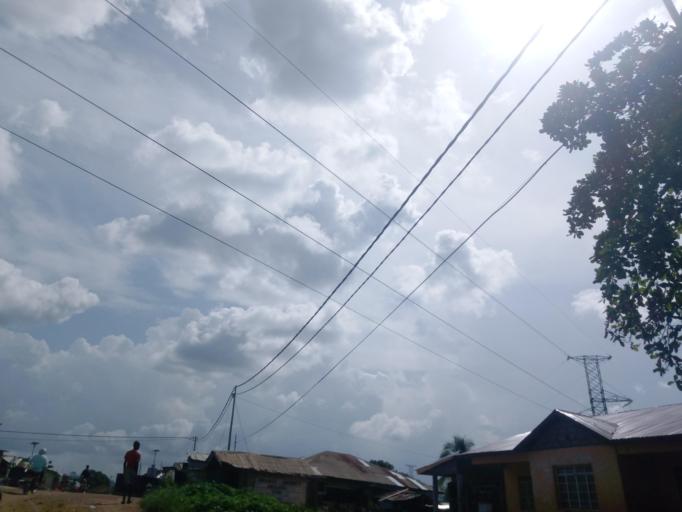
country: SL
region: Northern Province
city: Makeni
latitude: 8.8994
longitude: -12.0427
